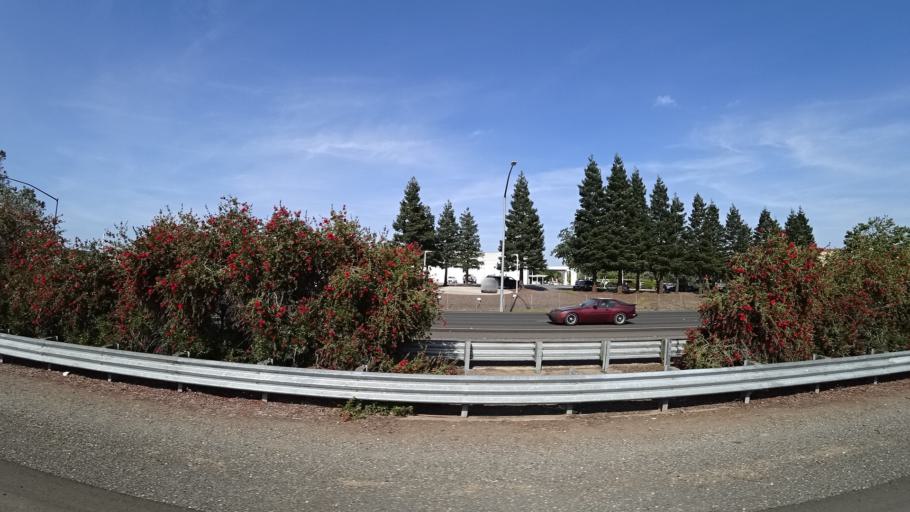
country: US
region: California
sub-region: Butte County
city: Chico
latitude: 39.7186
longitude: -121.8037
